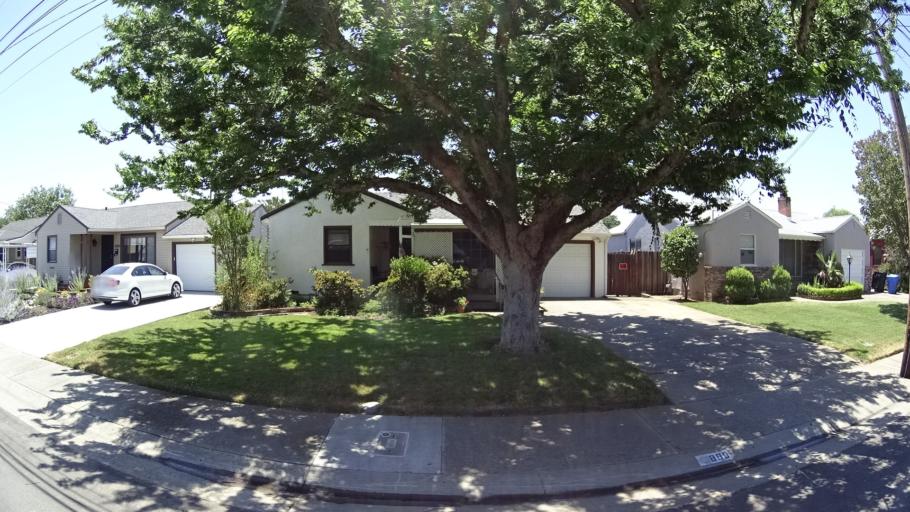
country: US
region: California
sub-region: Sacramento County
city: Parkway
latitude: 38.5350
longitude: -121.4374
